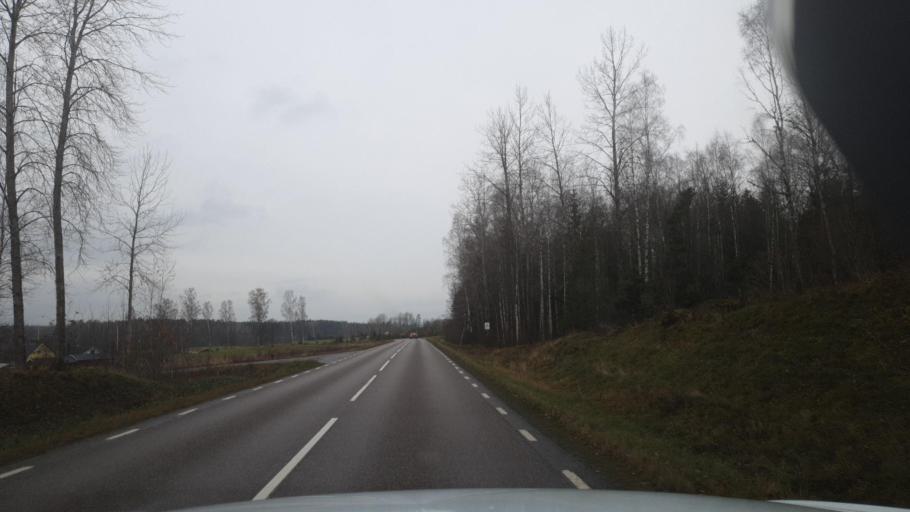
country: SE
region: Vaermland
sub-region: Arvika Kommun
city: Arvika
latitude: 59.5215
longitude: 12.6240
